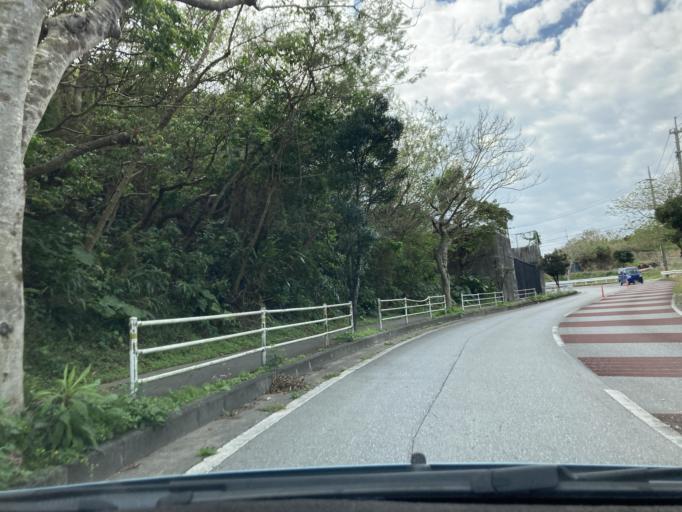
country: JP
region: Okinawa
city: Tomigusuku
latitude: 26.1838
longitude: 127.6947
